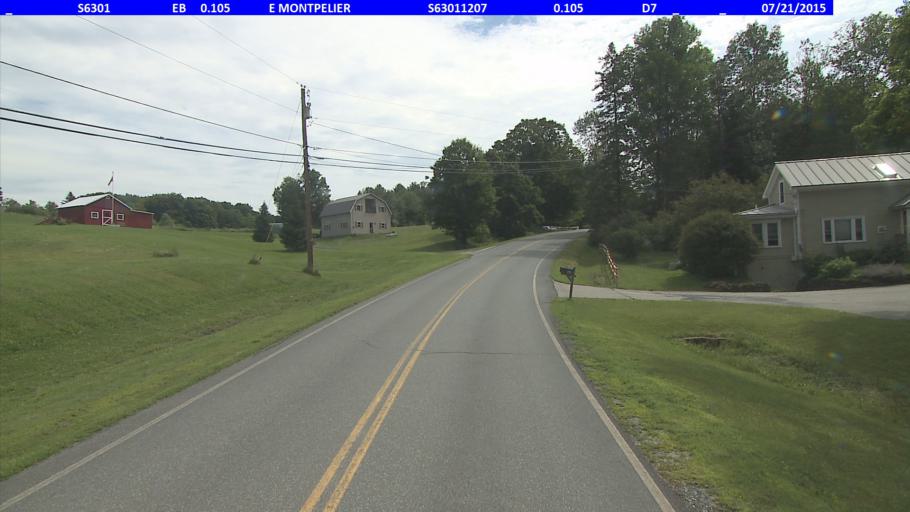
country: US
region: Vermont
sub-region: Washington County
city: Montpelier
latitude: 44.2745
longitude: -72.5523
